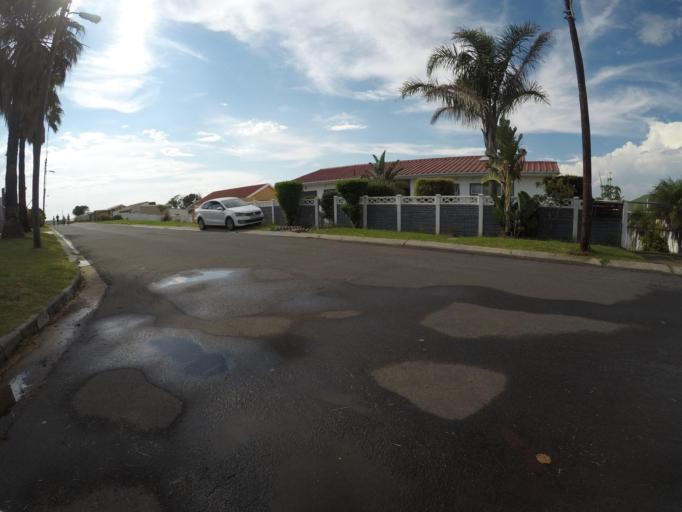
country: ZA
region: Eastern Cape
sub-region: Buffalo City Metropolitan Municipality
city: East London
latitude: -33.0218
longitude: 27.8733
